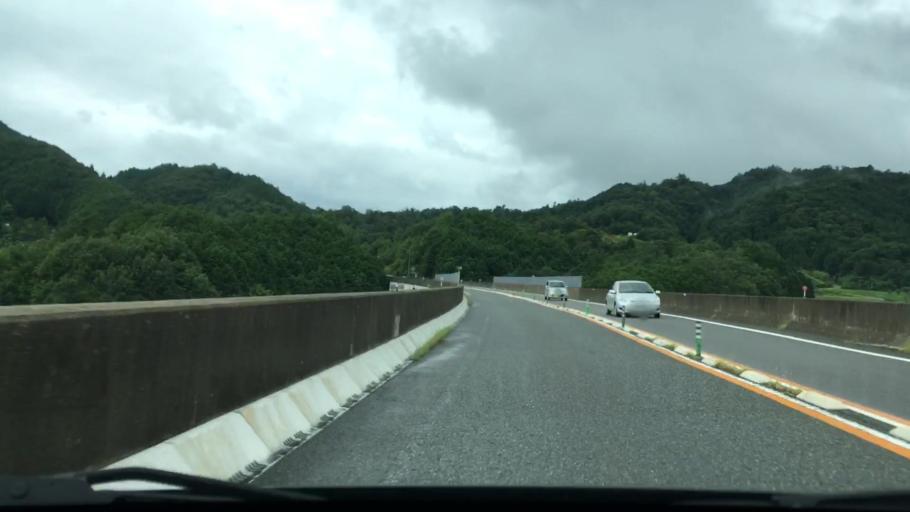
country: JP
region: Hyogo
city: Toyooka
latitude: 35.3097
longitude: 134.8266
